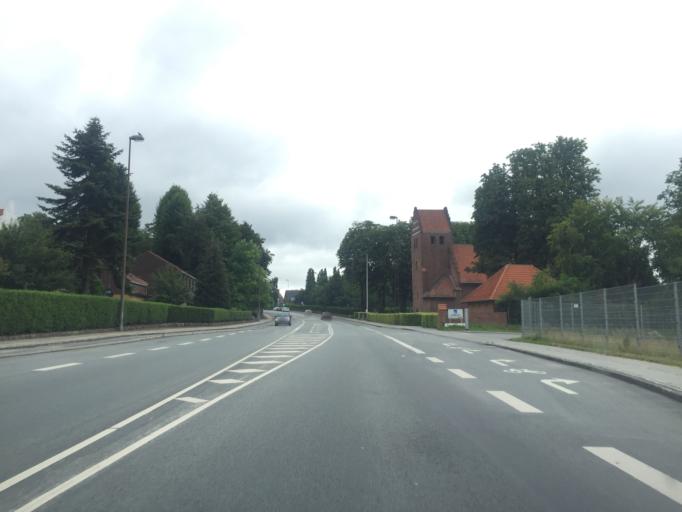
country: DK
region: South Denmark
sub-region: Odense Kommune
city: Odense
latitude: 55.3627
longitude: 10.3748
